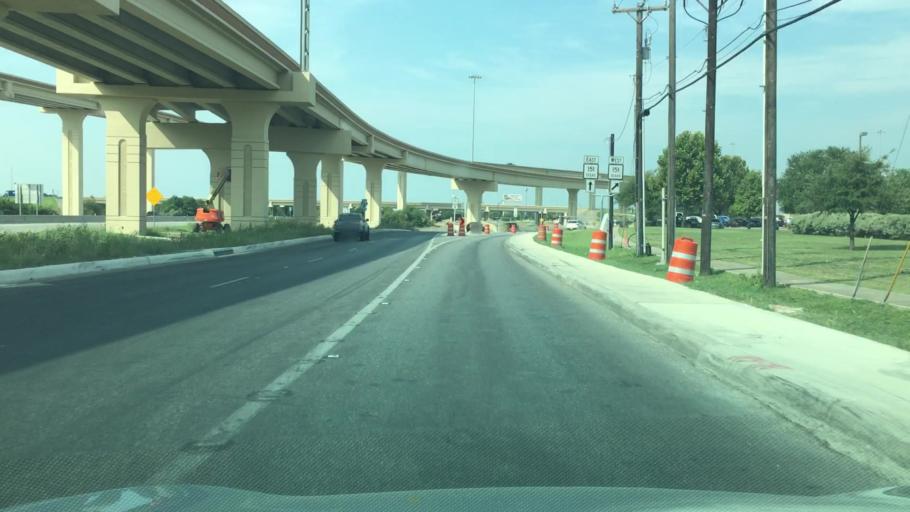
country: US
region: Texas
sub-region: Bexar County
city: Lackland Air Force Base
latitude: 29.4373
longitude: -98.6437
